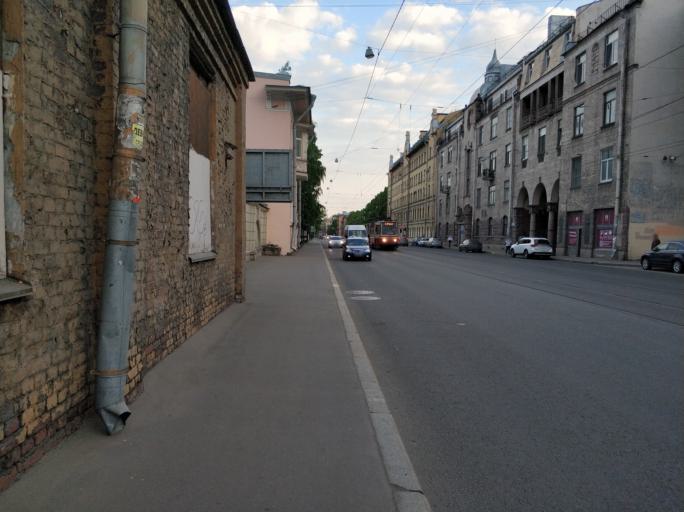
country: RU
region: Leningrad
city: Finlyandskiy
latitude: 59.9670
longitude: 30.3503
